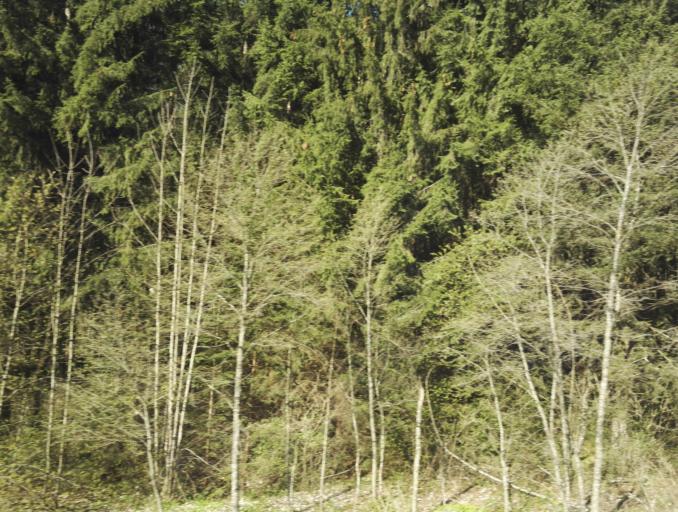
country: AT
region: Salzburg
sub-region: Politischer Bezirk Sankt Johann im Pongau
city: Forstau
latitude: 47.3946
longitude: 13.5912
